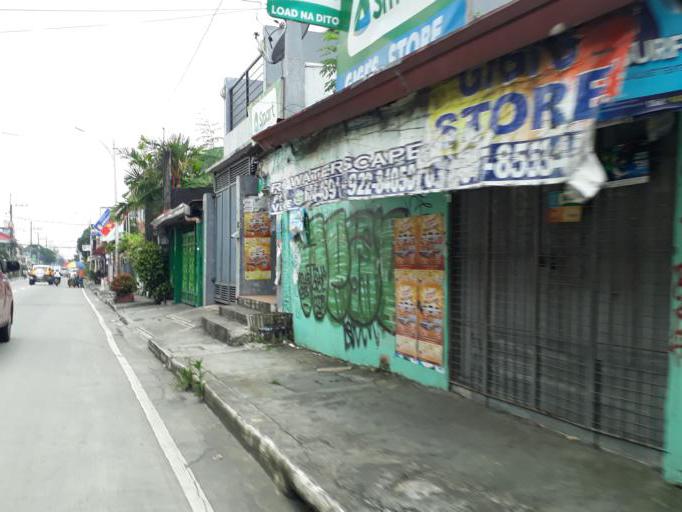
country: PH
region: Calabarzon
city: Bagong Pagasa
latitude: 14.6604
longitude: 121.0403
